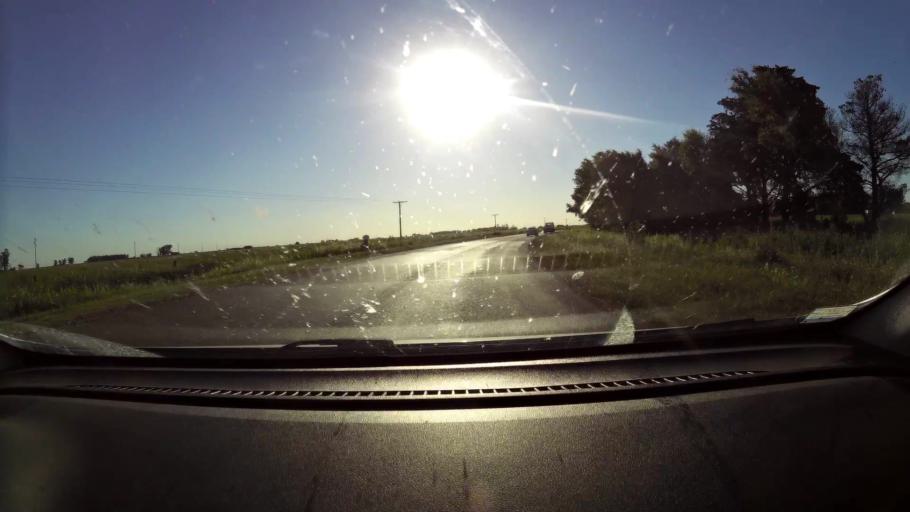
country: AR
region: Cordoba
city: Devoto
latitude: -31.5545
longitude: -62.2248
